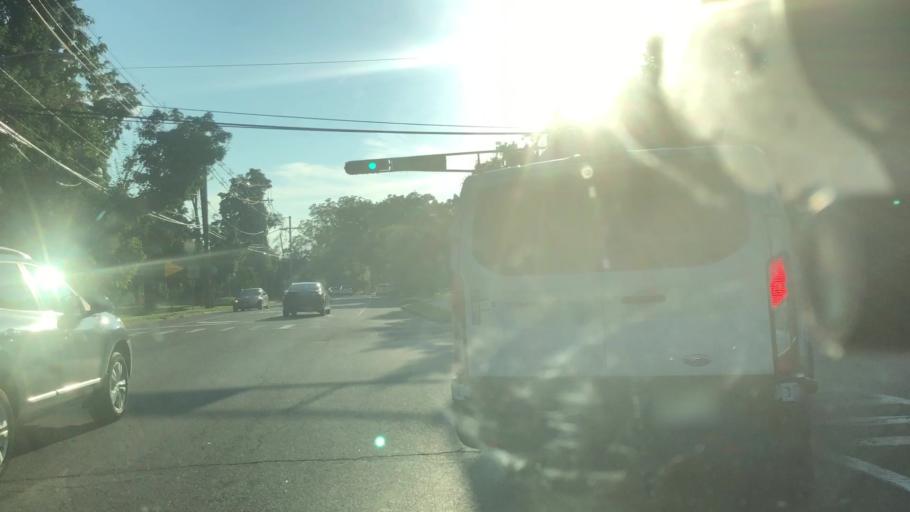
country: US
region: New Jersey
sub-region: Union County
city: Union
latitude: 40.6979
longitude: -74.2579
